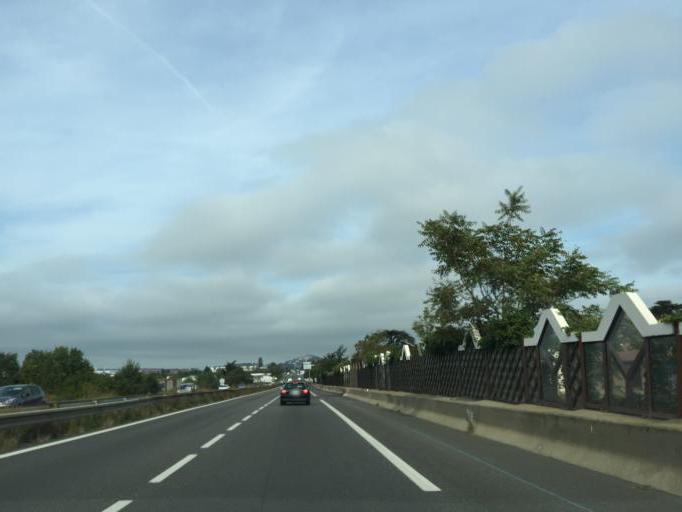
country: FR
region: Rhone-Alpes
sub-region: Departement de la Loire
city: Saint-Etienne
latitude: 45.4533
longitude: 4.4155
